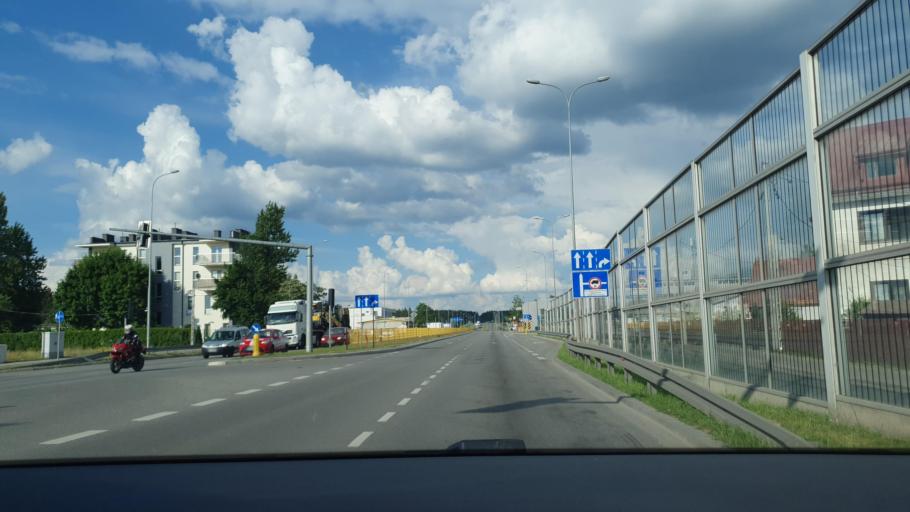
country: PL
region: Podlasie
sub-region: Bialystok
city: Bialystok
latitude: 53.1239
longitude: 23.2081
